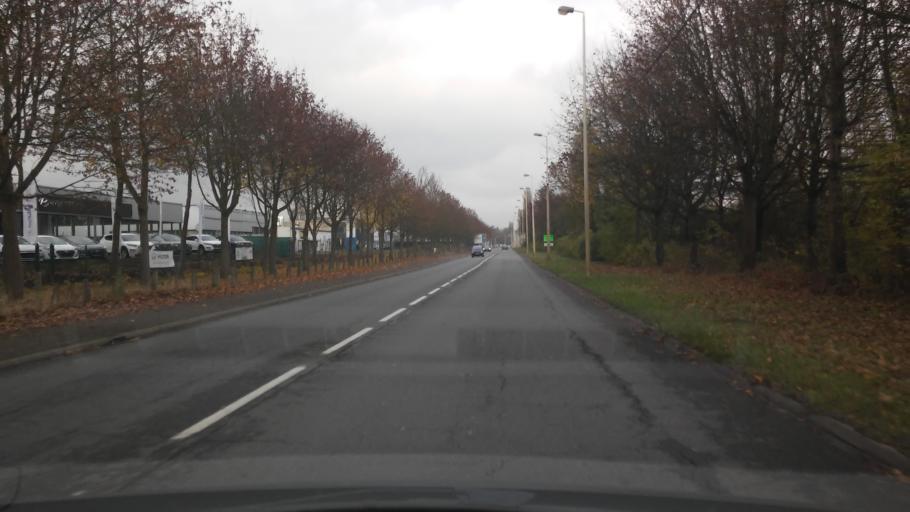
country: FR
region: Lorraine
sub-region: Departement de la Moselle
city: Terville
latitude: 49.3382
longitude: 6.1591
